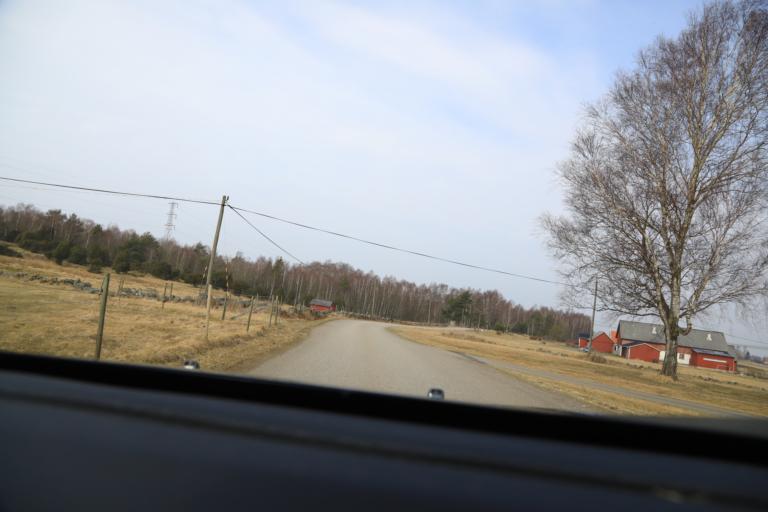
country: SE
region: Halland
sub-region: Kungsbacka Kommun
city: Frillesas
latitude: 57.2701
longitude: 12.1528
